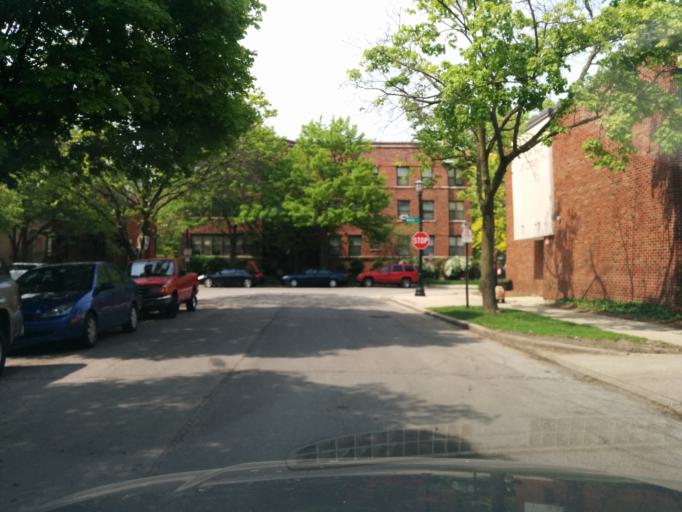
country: US
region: Illinois
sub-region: Cook County
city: Evanston
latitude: 42.0336
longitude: -87.6841
